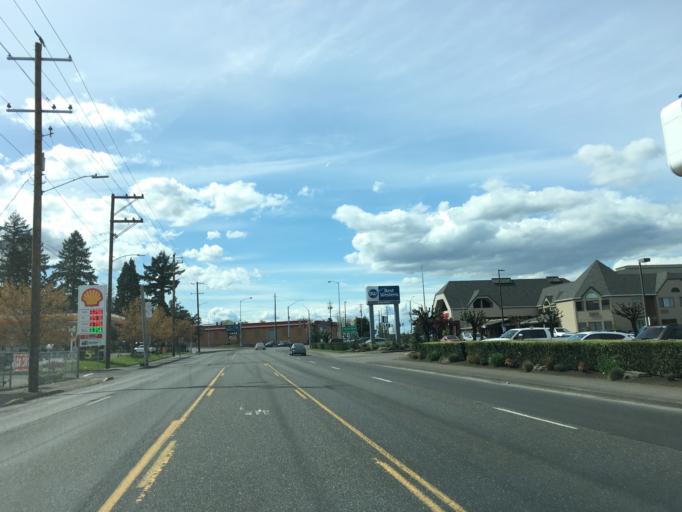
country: US
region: Oregon
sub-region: Multnomah County
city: Lents
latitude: 45.5592
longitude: -122.5591
